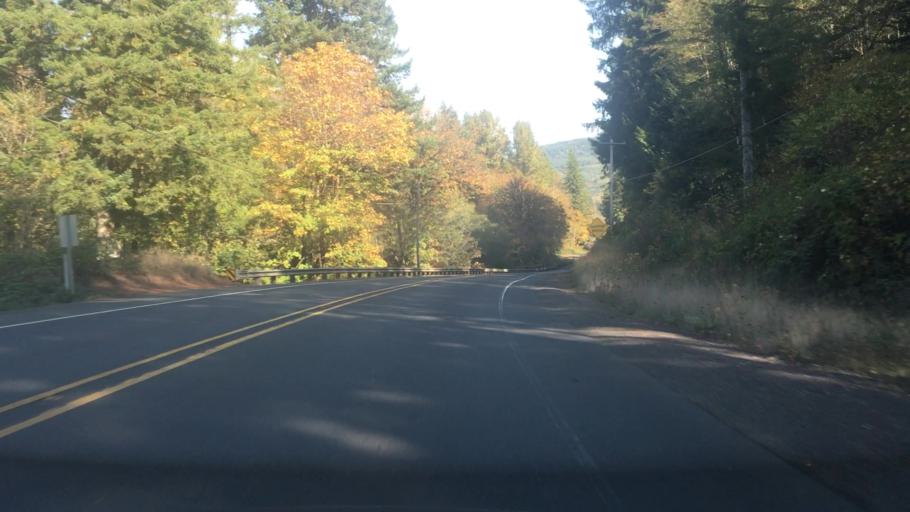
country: US
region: Oregon
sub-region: Lincoln County
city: Rose Lodge
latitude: 45.0183
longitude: -123.8694
